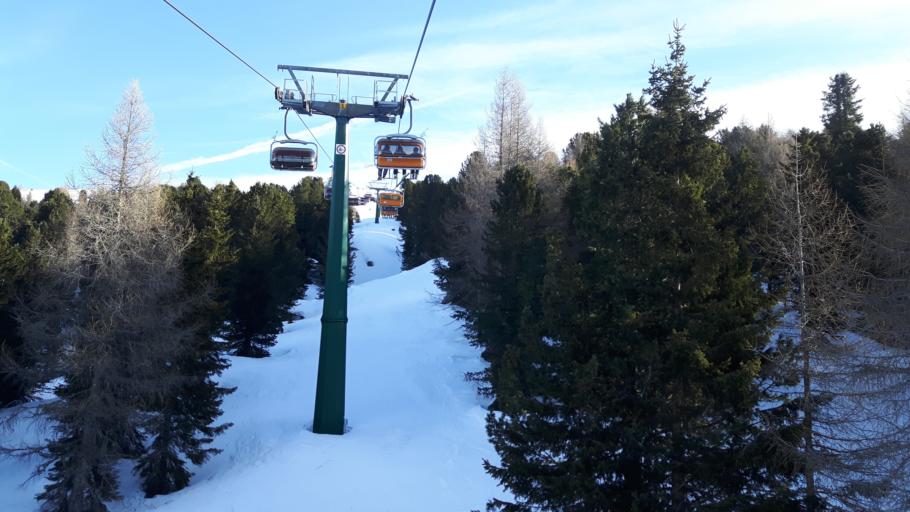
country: IT
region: Trentino-Alto Adige
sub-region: Provincia di Trento
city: Moena
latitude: 46.3373
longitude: 11.7094
